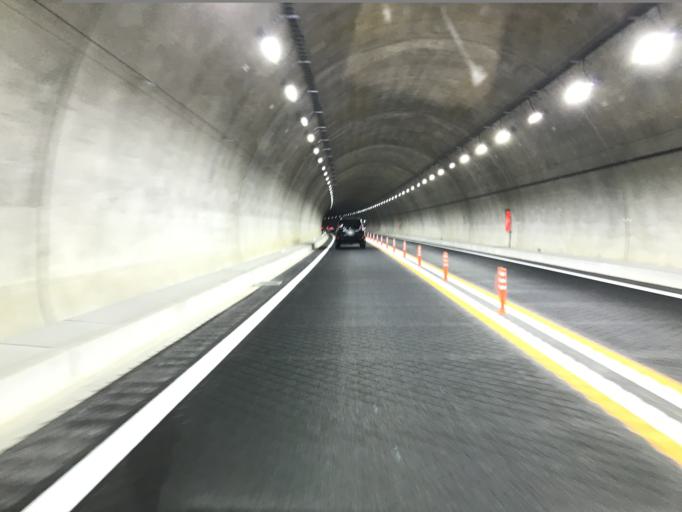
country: JP
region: Yamagata
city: Kaminoyama
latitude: 38.1720
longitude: 140.3106
